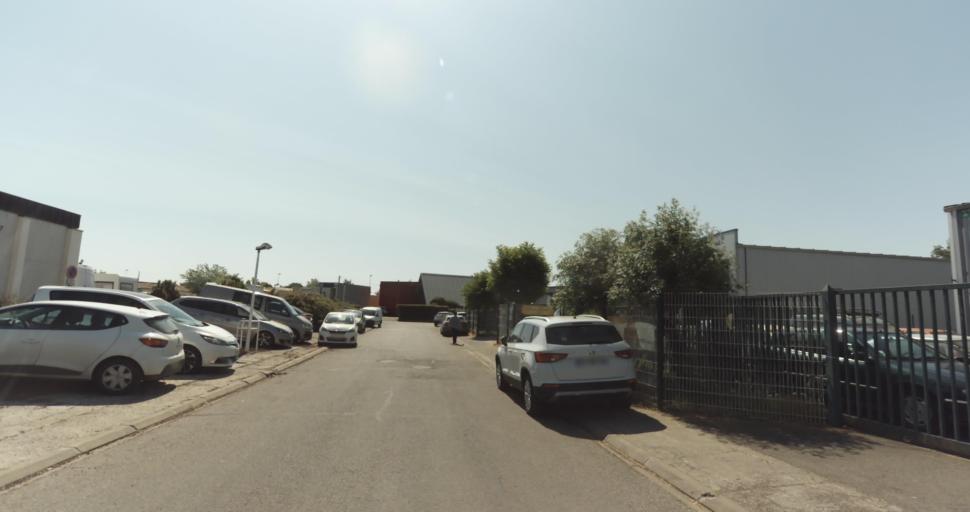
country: FR
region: Midi-Pyrenees
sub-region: Departement de la Haute-Garonne
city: La Salvetat-Saint-Gilles
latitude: 43.5829
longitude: 1.2738
